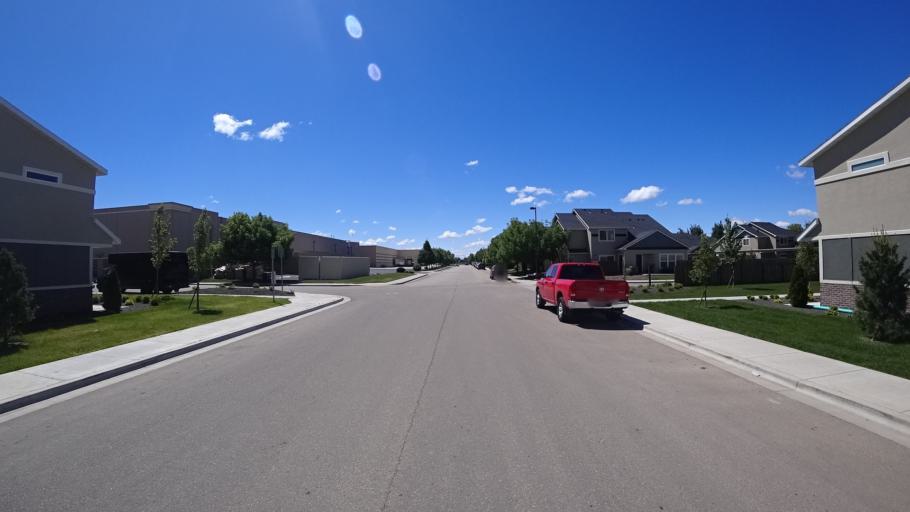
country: US
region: Idaho
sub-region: Ada County
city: Meridian
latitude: 43.6377
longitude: -116.3586
